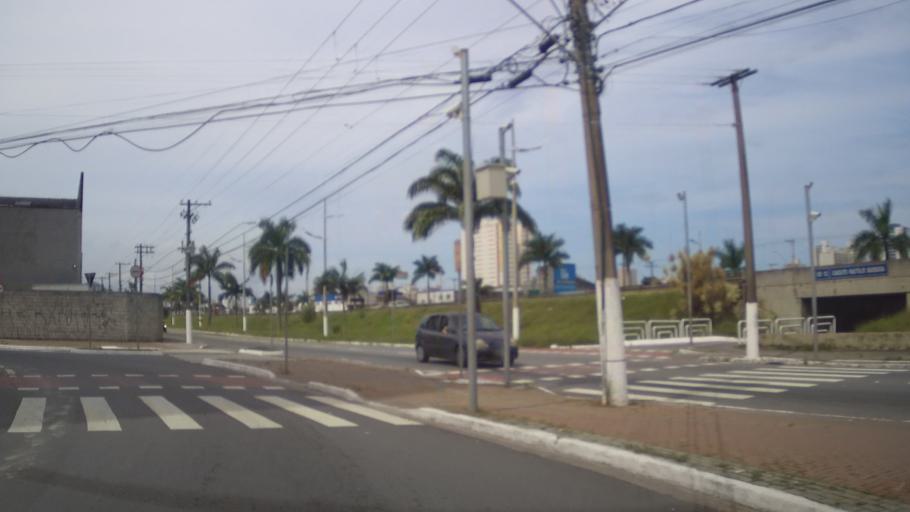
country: BR
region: Sao Paulo
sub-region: Praia Grande
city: Praia Grande
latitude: -24.0146
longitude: -46.4596
